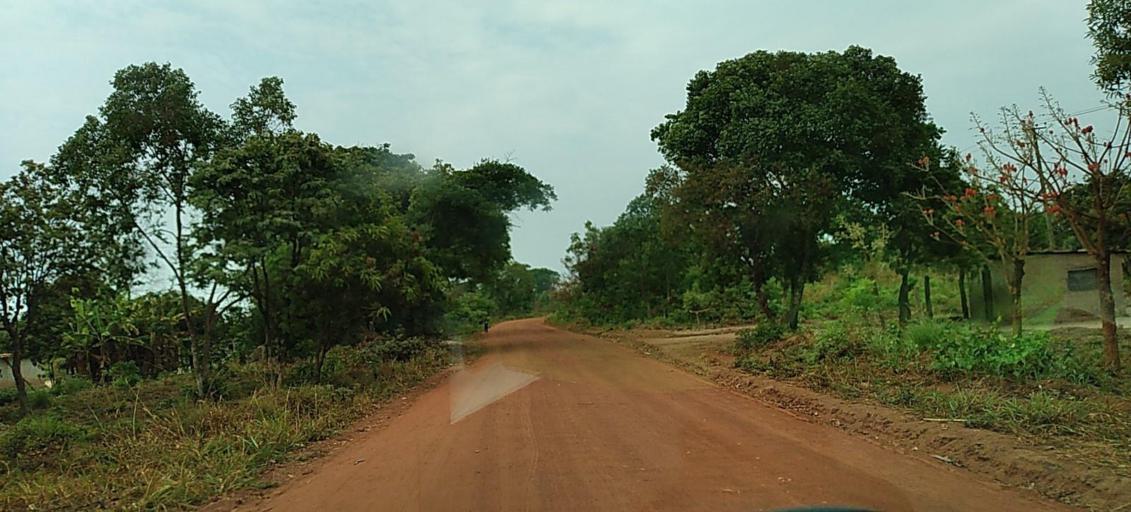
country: ZM
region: North-Western
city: Solwezi
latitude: -12.2408
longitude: 26.5119
